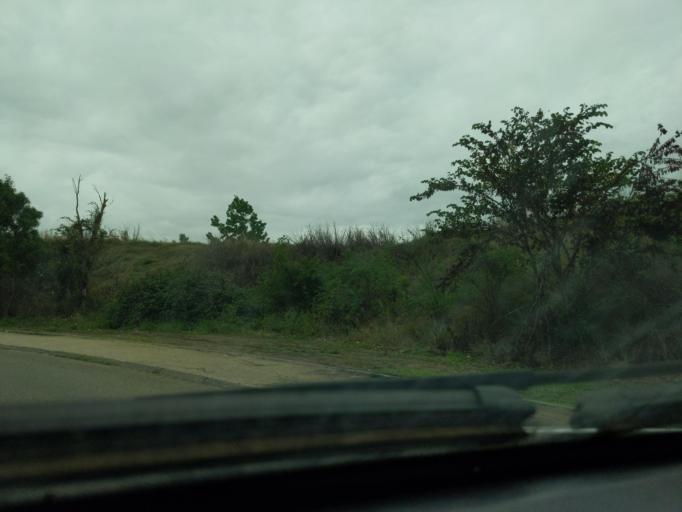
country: FR
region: Midi-Pyrenees
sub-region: Departement de la Haute-Garonne
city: Cugnaux
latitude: 43.5732
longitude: 1.3680
